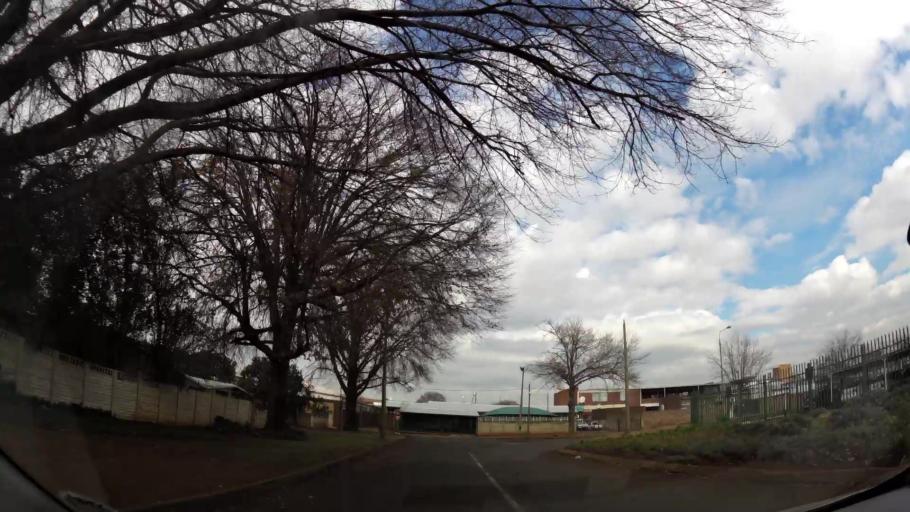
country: ZA
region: Gauteng
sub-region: Sedibeng District Municipality
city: Meyerton
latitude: -26.5582
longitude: 28.0170
